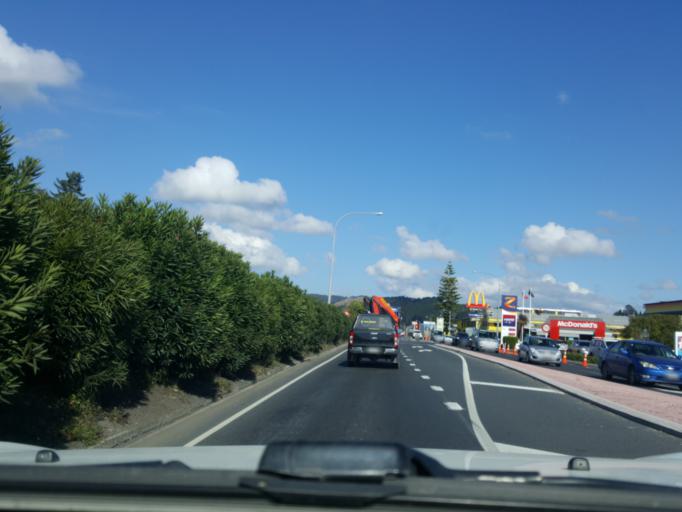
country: NZ
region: Waikato
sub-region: Waikato District
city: Ngaruawahia
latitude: -37.5669
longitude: 175.1589
